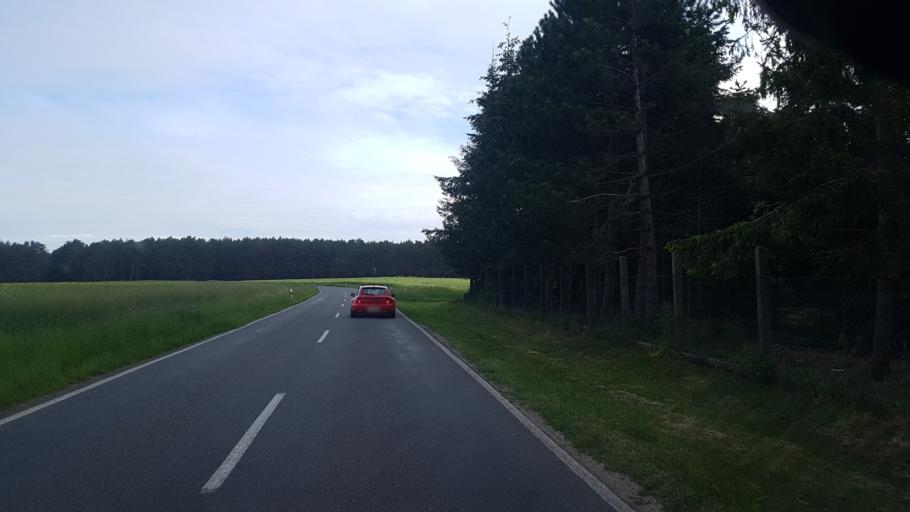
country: DE
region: Brandenburg
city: Baruth
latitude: 51.9893
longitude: 13.4820
